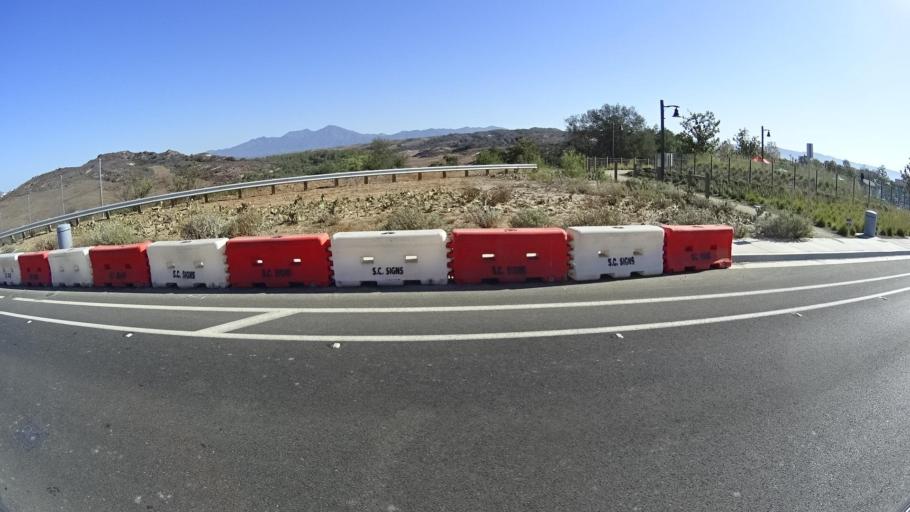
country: US
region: California
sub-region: Orange County
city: Ladera Ranch
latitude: 33.5231
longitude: -117.5925
